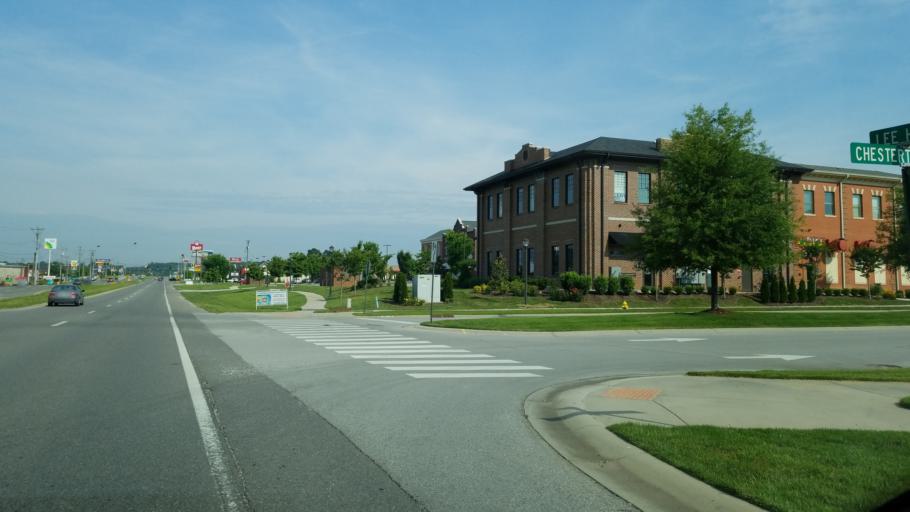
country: US
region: Tennessee
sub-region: Hamilton County
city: Collegedale
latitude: 35.0815
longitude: -85.0545
